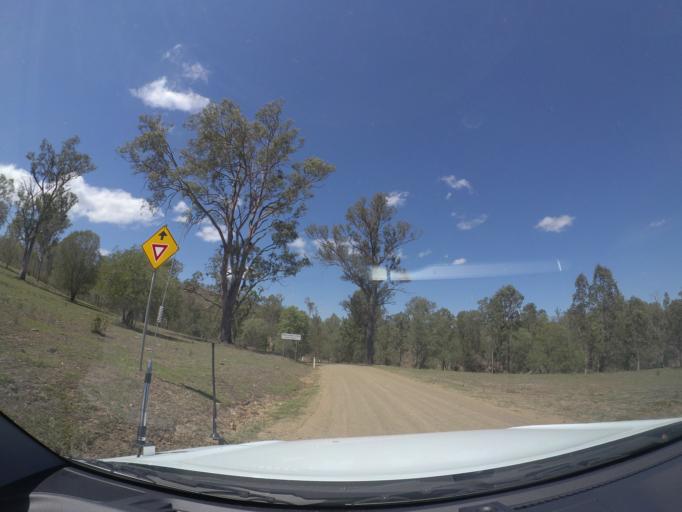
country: AU
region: Queensland
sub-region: Logan
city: Cedar Vale
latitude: -27.8582
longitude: 152.8613
